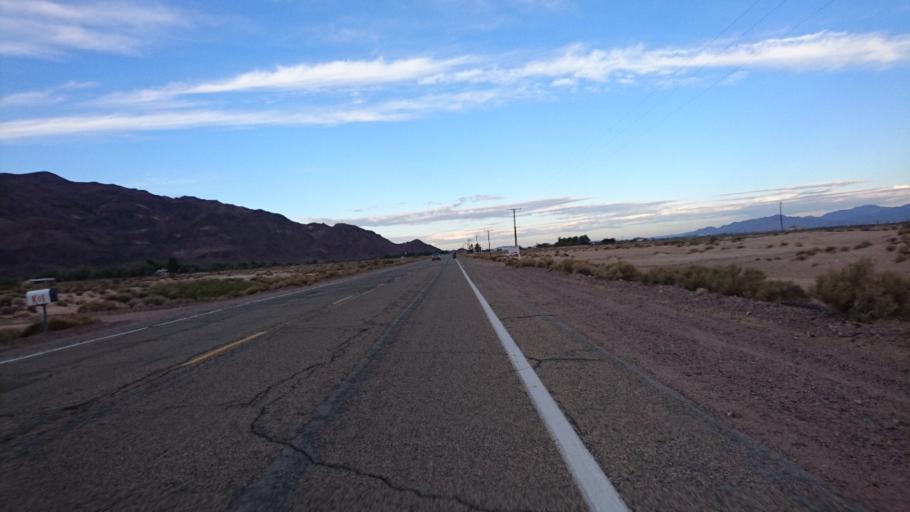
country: US
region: California
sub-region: San Bernardino County
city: Barstow
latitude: 34.8206
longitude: -116.6497
